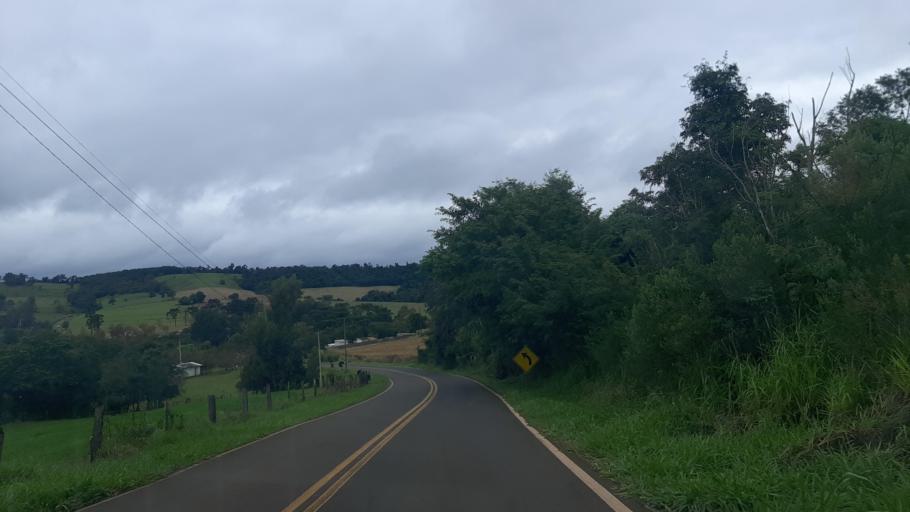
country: BR
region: Parana
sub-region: Ampere
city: Ampere
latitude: -25.9726
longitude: -53.4434
